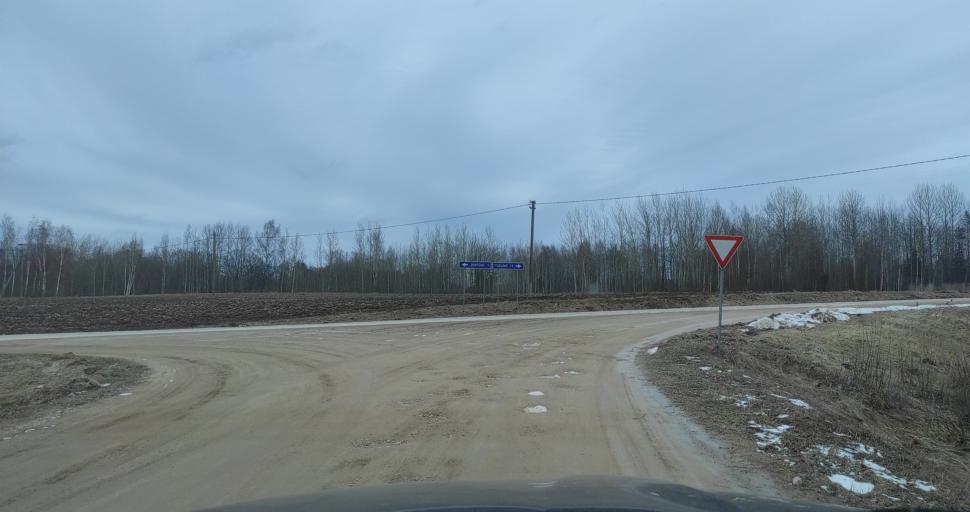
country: LV
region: Tukuma Rajons
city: Tukums
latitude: 57.0863
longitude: 23.0861
